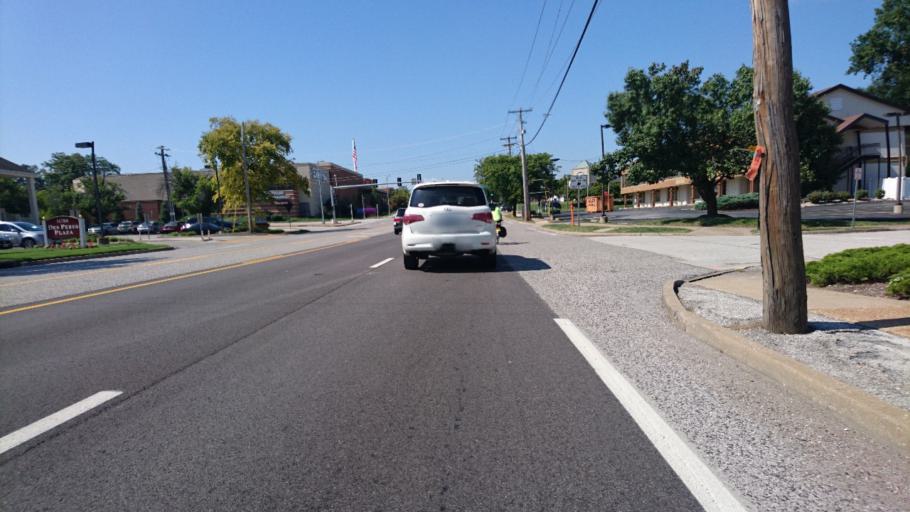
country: US
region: Missouri
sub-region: Saint Louis County
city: Des Peres
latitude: 38.6009
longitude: -90.4307
